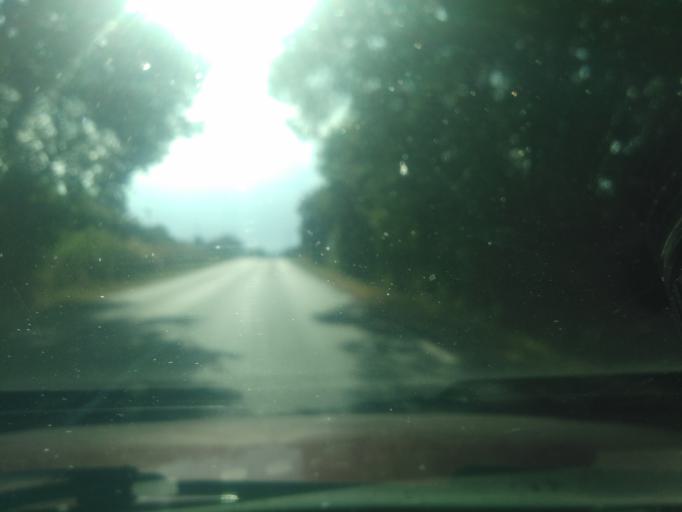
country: FR
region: Pays de la Loire
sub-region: Departement de la Vendee
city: Bazoges-en-Pareds
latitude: 46.6769
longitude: -0.8886
